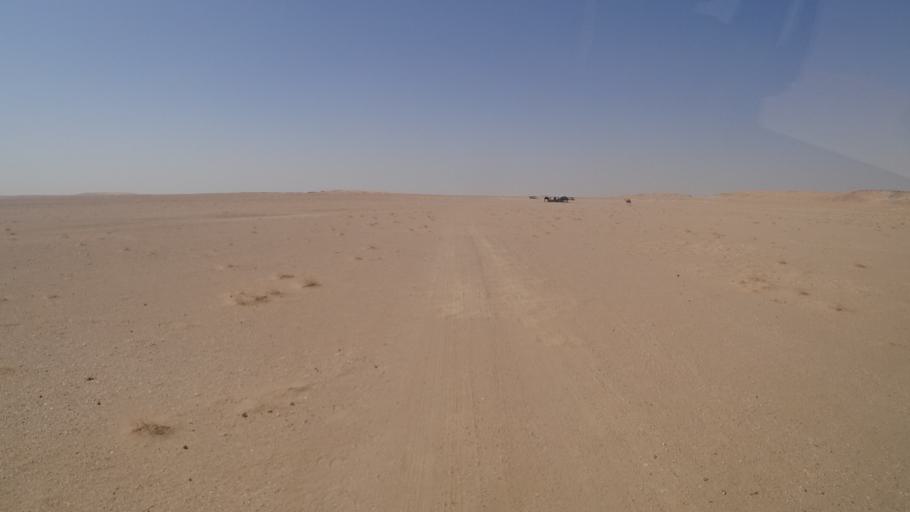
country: YE
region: Al Mahrah
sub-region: Shahan
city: Shihan as Sufla
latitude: 18.5759
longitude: 52.4986
